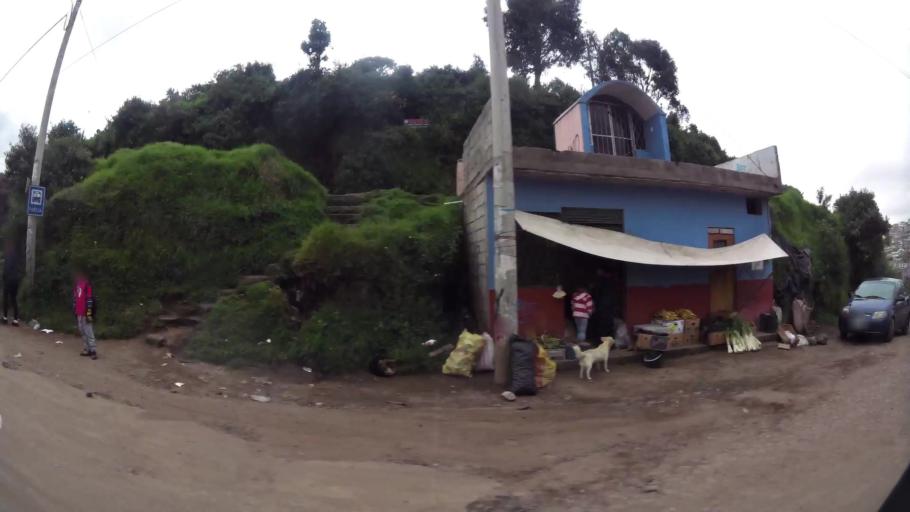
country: EC
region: Pichincha
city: Sangolqui
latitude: -0.3186
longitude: -78.5292
